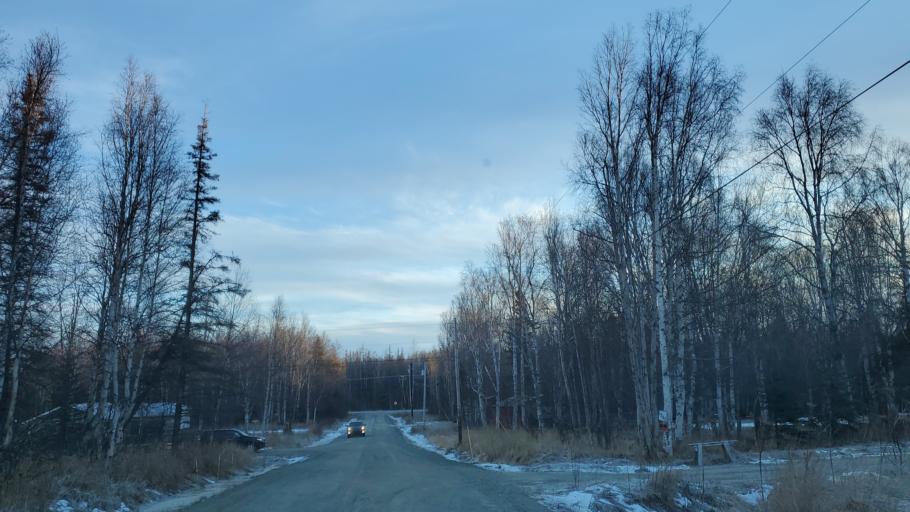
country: US
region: Alaska
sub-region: Matanuska-Susitna Borough
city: Lakes
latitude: 61.6518
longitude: -149.3174
